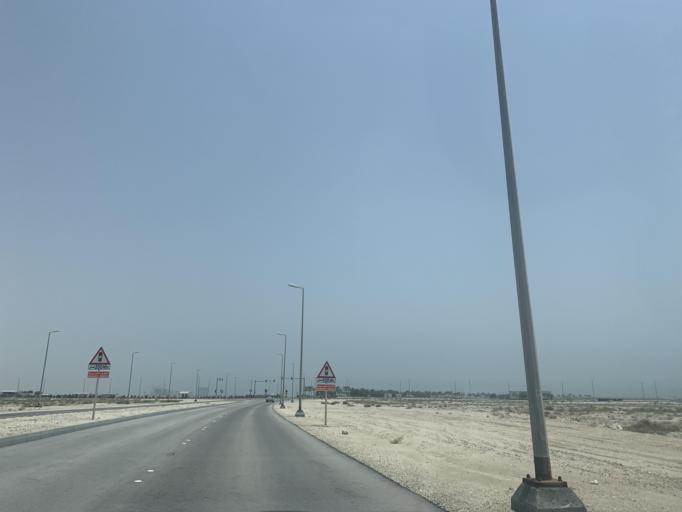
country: BH
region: Central Governorate
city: Dar Kulayb
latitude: 25.8440
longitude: 50.5940
